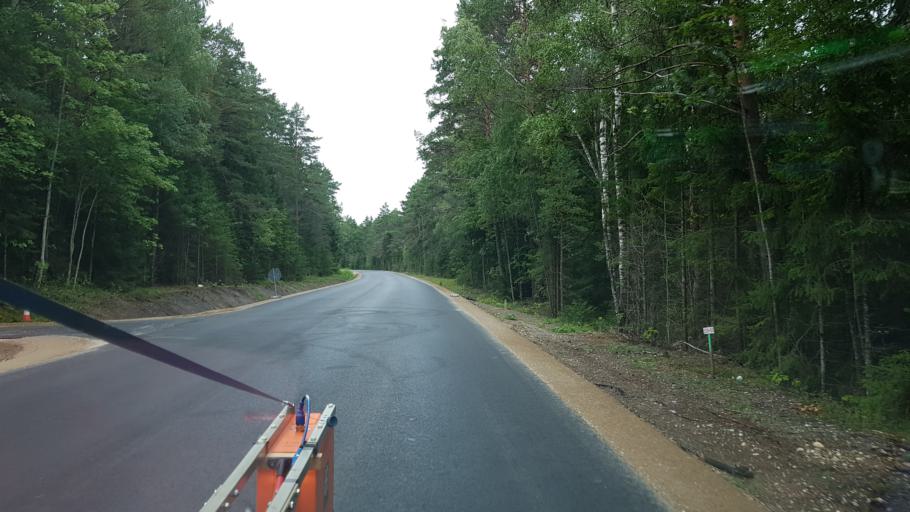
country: EE
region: Harju
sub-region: Nissi vald
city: Turba
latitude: 59.1291
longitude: 24.0697
